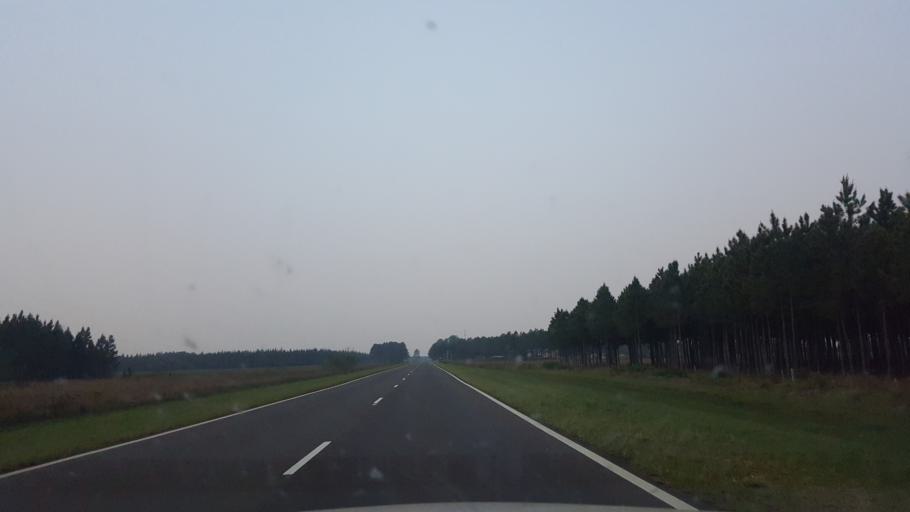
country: PY
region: Misiones
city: Ayolas
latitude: -27.6239
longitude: -56.9352
